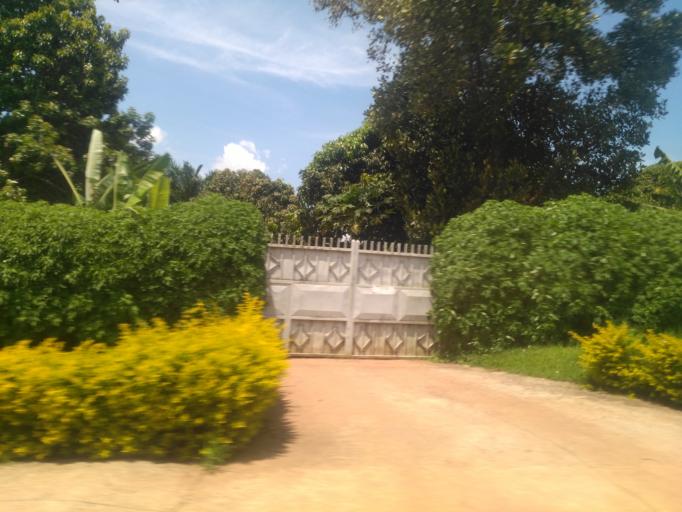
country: UG
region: Central Region
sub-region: Wakiso District
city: Entebbe
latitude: 0.0437
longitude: 32.4631
